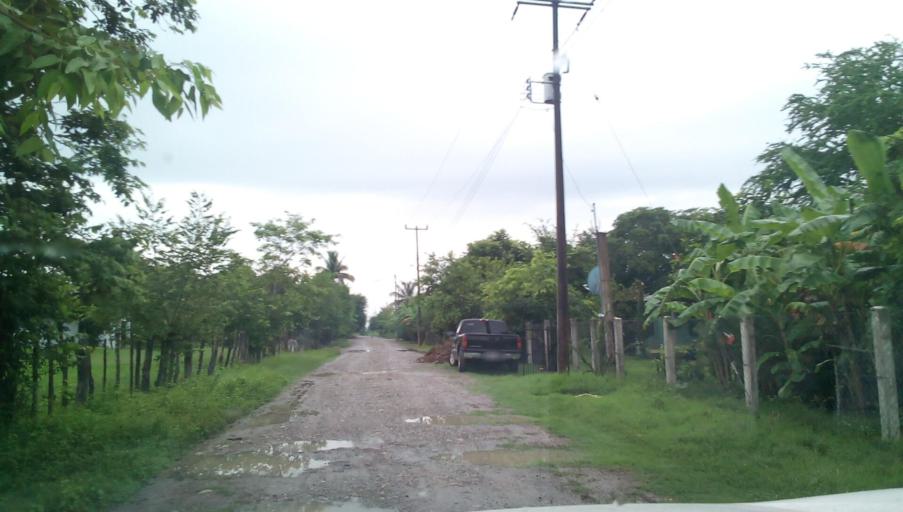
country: MX
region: Veracruz
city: Tempoal de Sanchez
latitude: 21.4182
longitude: -98.4306
